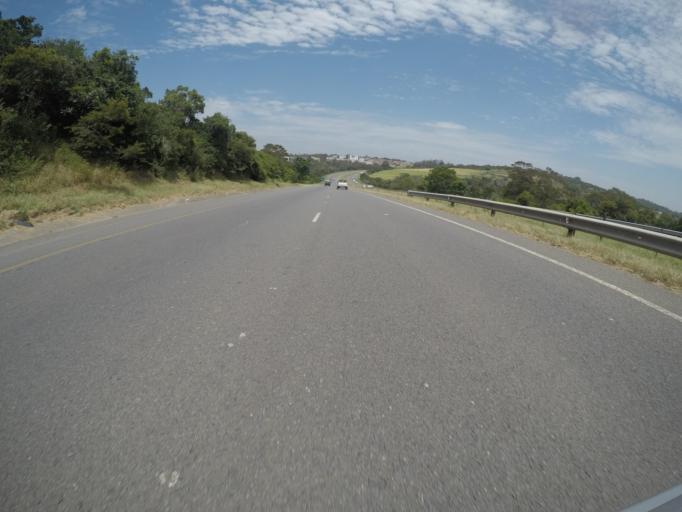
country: ZA
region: Eastern Cape
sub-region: Buffalo City Metropolitan Municipality
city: East London
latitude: -32.9427
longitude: 27.9433
